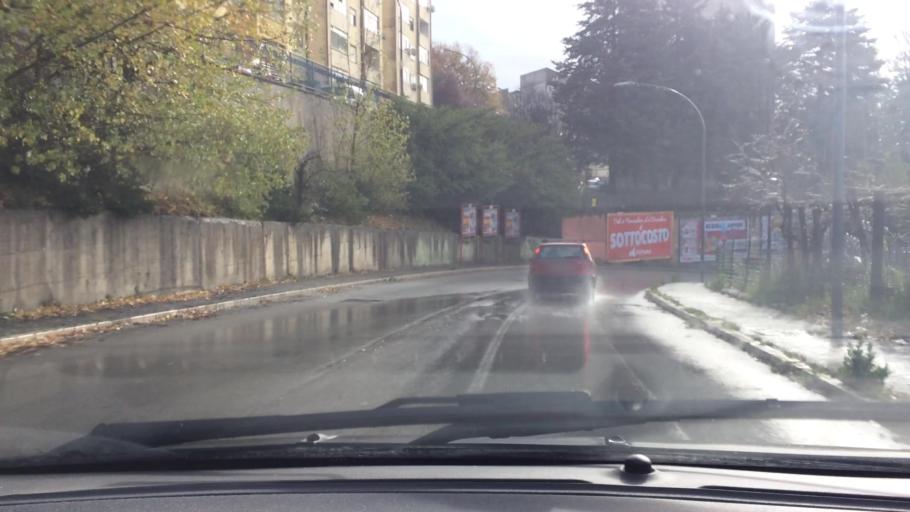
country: IT
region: Basilicate
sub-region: Provincia di Potenza
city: Potenza
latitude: 40.6341
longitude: 15.7887
